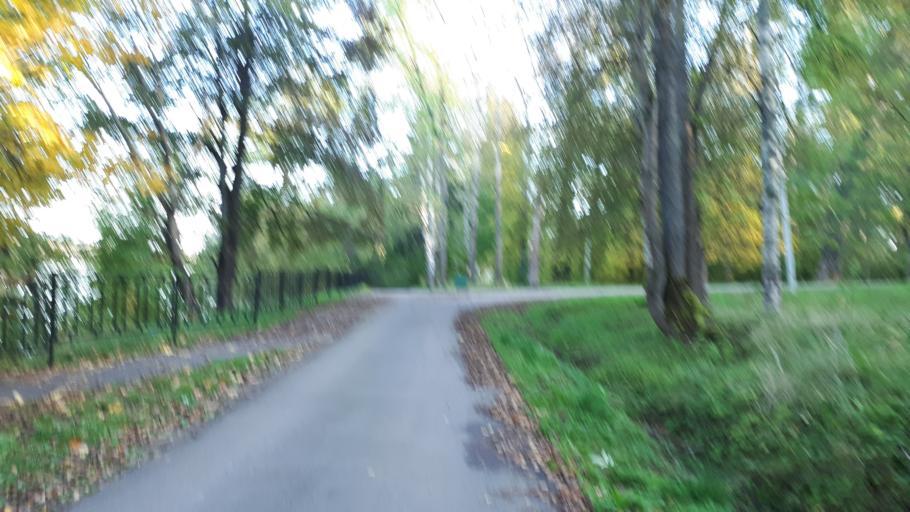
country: RU
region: Jaroslavl
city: Konstantinovskiy
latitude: 57.8300
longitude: 39.6017
